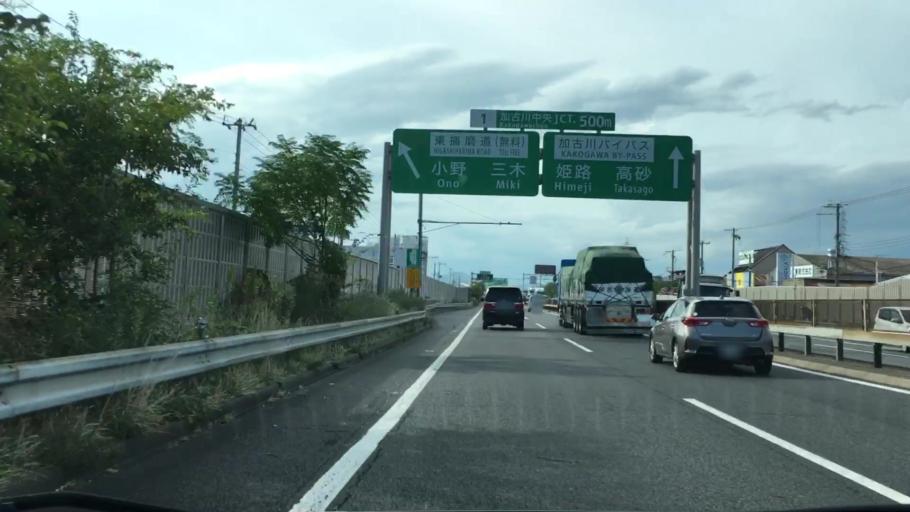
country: JP
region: Hyogo
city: Kakogawacho-honmachi
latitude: 34.7562
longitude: 134.8609
